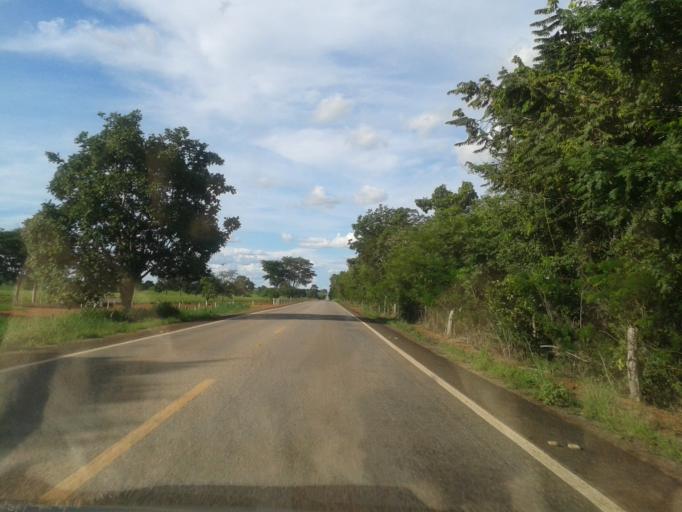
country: BR
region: Goias
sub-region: Mozarlandia
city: Mozarlandia
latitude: -14.2838
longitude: -50.4014
